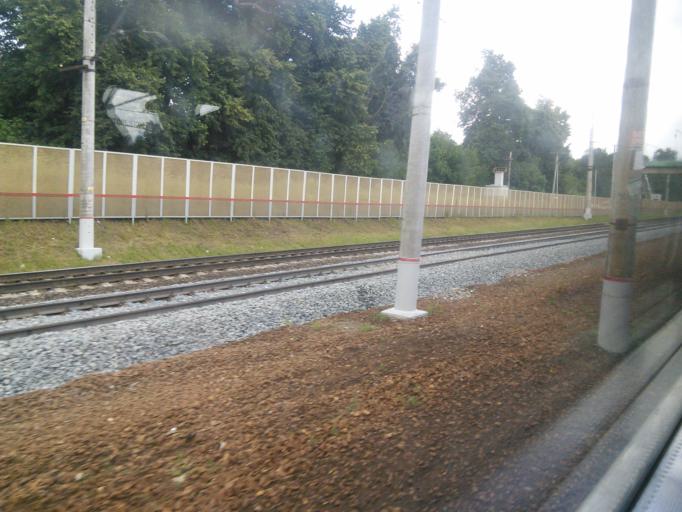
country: RU
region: Moskovskaya
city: Vereya
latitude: 55.6354
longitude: 38.0430
